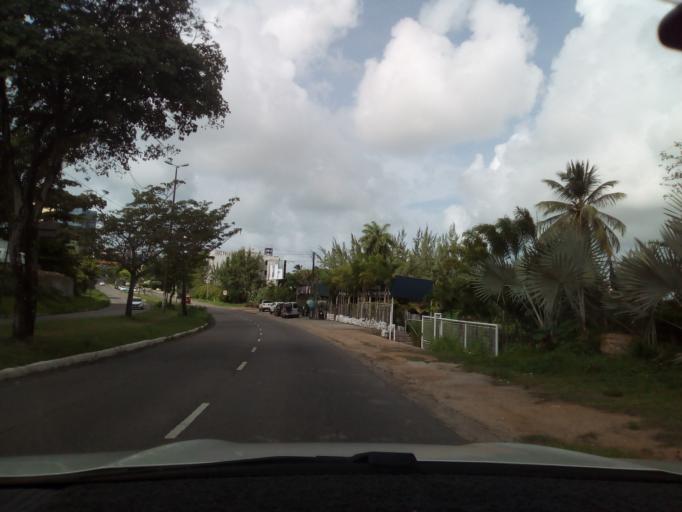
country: BR
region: Paraiba
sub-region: Joao Pessoa
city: Joao Pessoa
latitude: -7.1271
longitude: -34.8511
